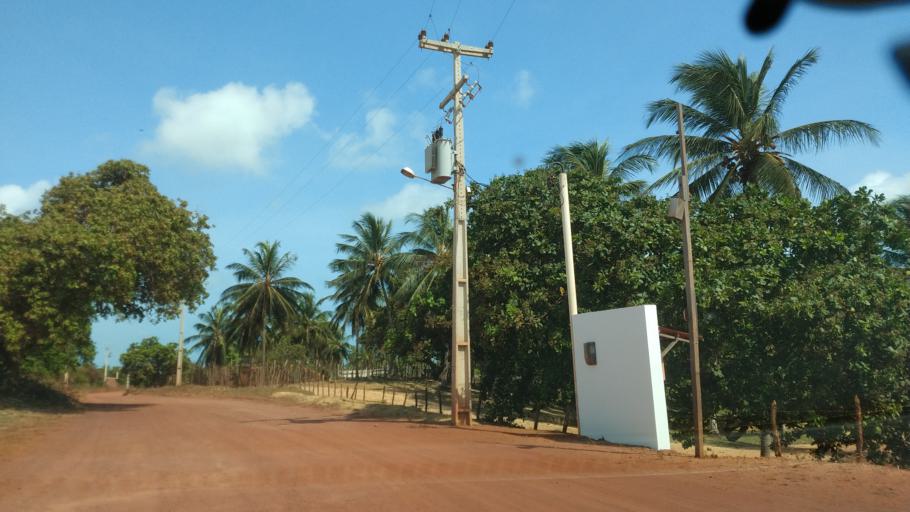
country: BR
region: Rio Grande do Norte
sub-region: Touros
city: Touros
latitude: -5.1598
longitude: -35.4953
